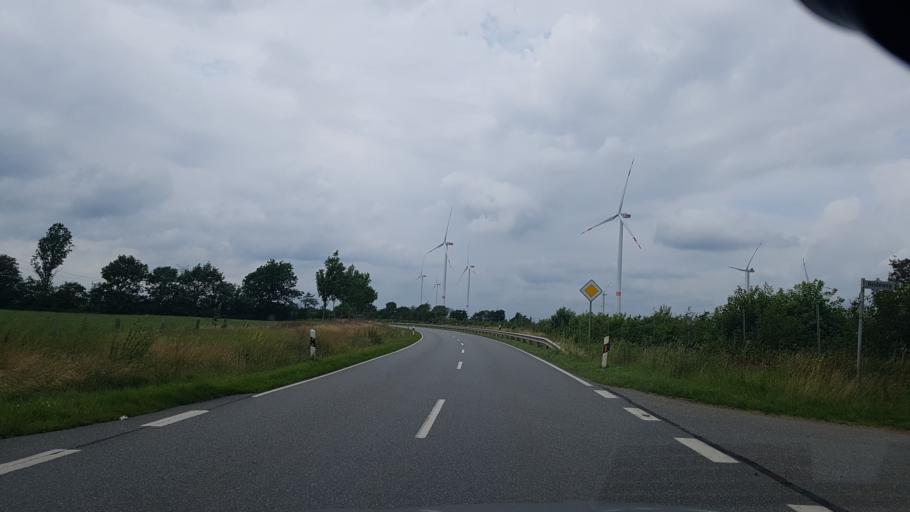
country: DE
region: Schleswig-Holstein
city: Jardelund
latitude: 54.8409
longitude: 9.2103
